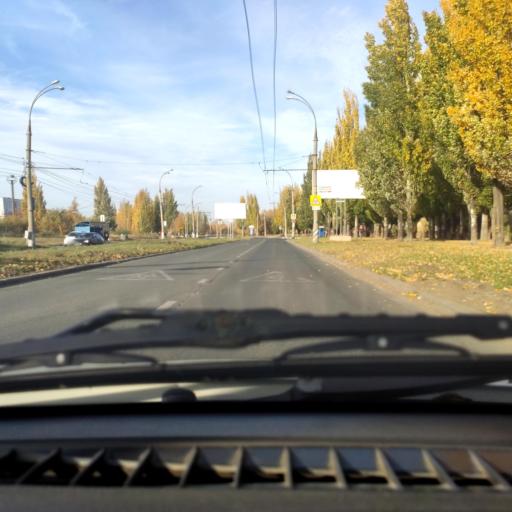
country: RU
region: Samara
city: Tol'yatti
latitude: 53.5403
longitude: 49.2791
